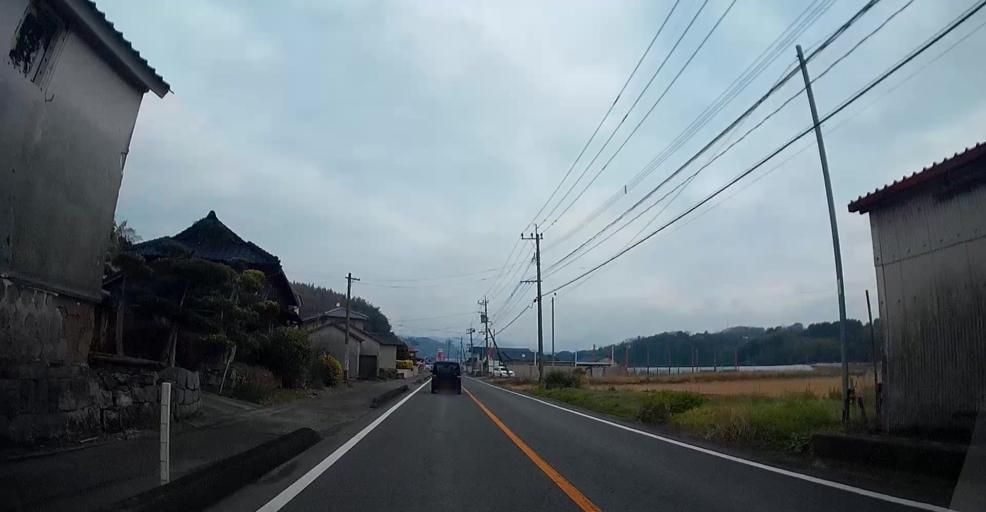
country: JP
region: Kumamoto
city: Yatsushiro
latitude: 32.6206
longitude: 130.5133
